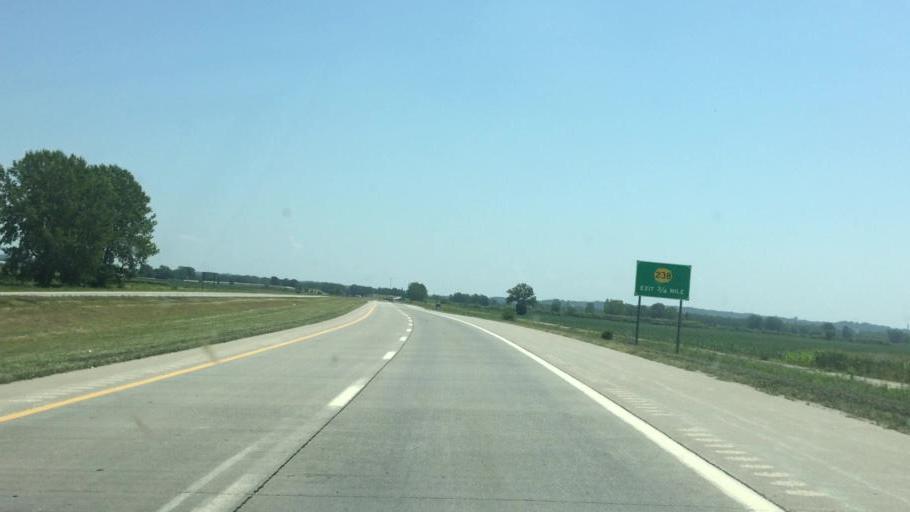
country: US
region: Kansas
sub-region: Doniphan County
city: Wathena
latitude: 39.7404
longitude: -94.9133
